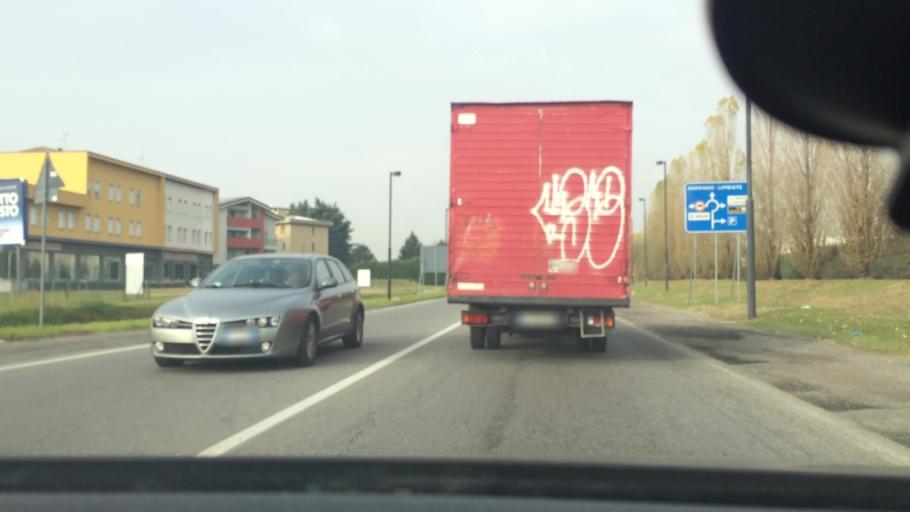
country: IT
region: Lombardy
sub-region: Provincia di Monza e Brianza
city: Varedo
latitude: 45.6000
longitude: 9.1661
